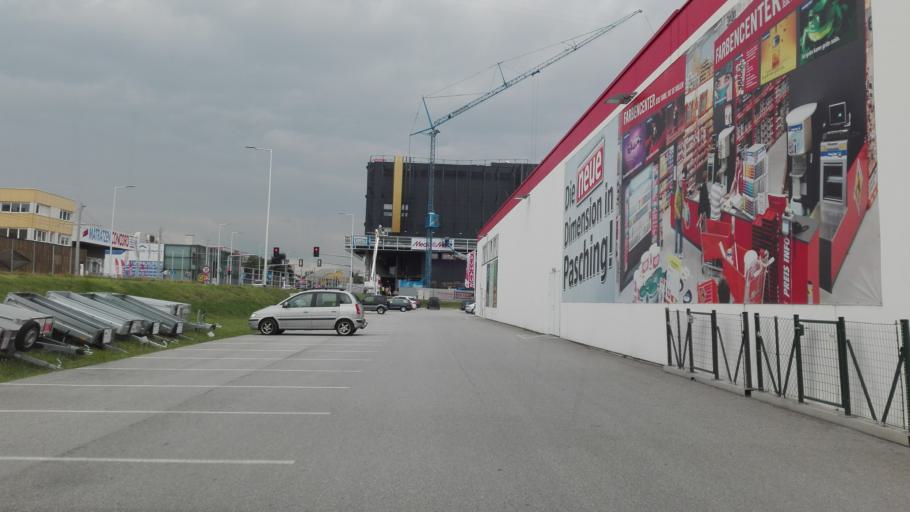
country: AT
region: Upper Austria
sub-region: Politischer Bezirk Linz-Land
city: Traun
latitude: 48.2456
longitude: 14.2390
